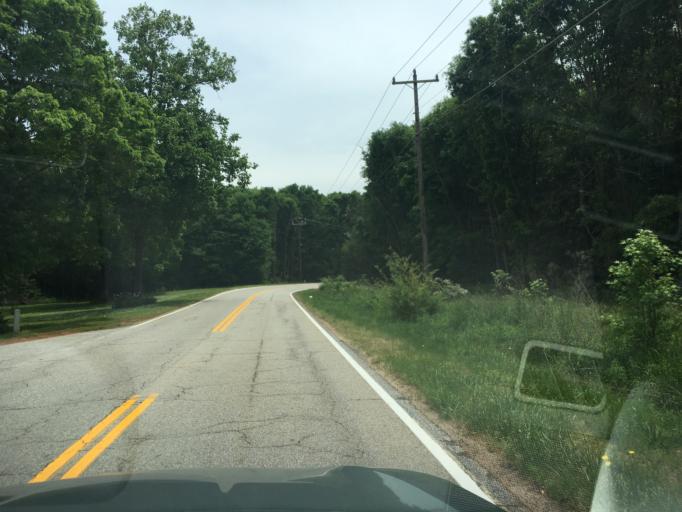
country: US
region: South Carolina
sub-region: Spartanburg County
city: Fairforest
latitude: 34.9733
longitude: -82.0113
